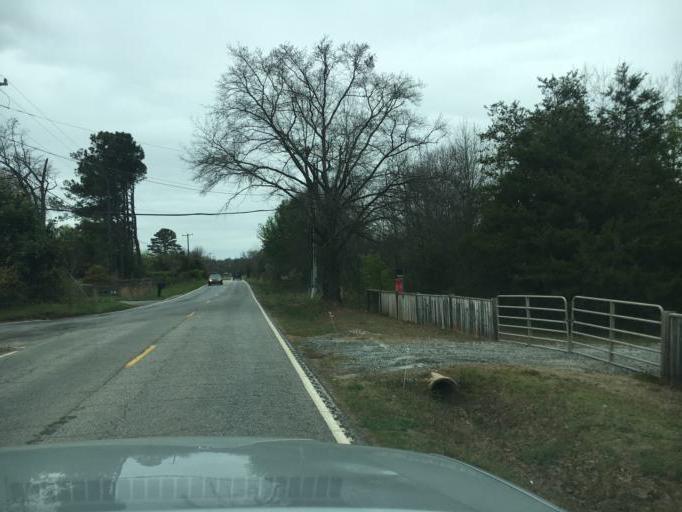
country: US
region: South Carolina
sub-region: Spartanburg County
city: Duncan
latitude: 34.9944
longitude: -82.1768
